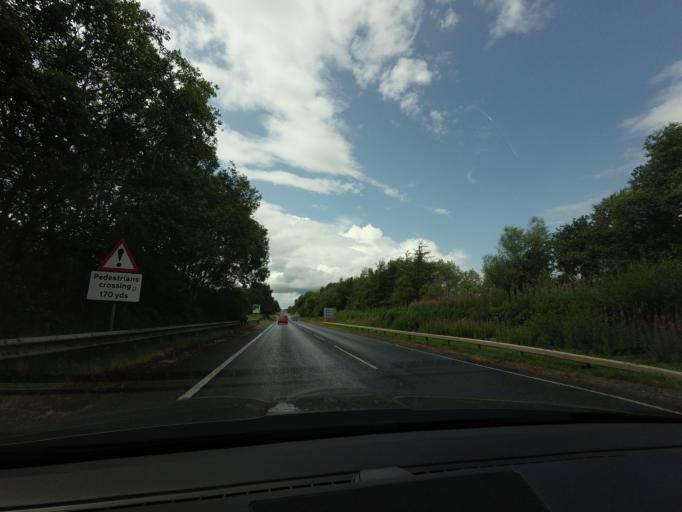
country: GB
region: Scotland
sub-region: Moray
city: Lhanbryd
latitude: 57.6331
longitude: -3.2188
